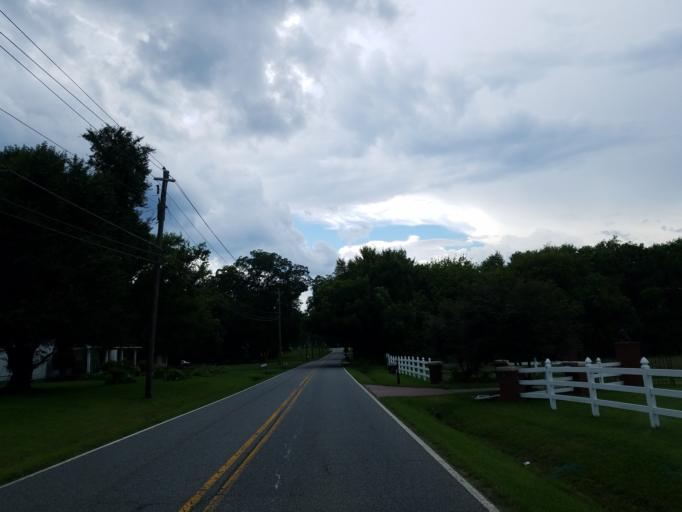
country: US
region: Georgia
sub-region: Bartow County
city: Cartersville
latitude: 34.2494
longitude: -84.8498
